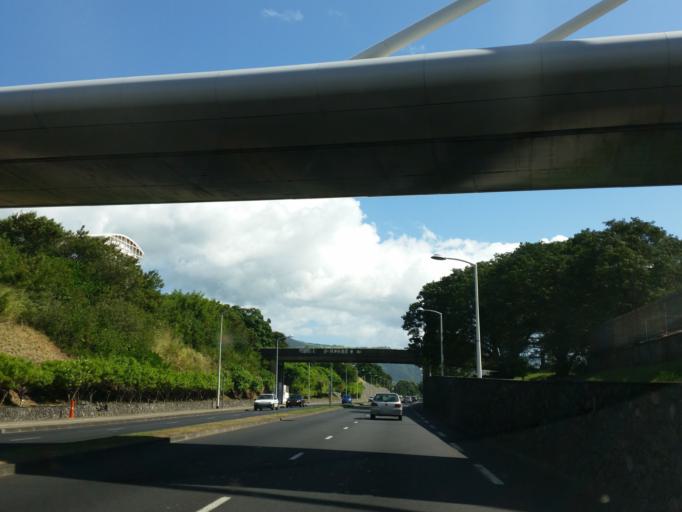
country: RE
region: Reunion
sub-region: Reunion
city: Saint-Denis
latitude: -20.9006
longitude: 55.4866
